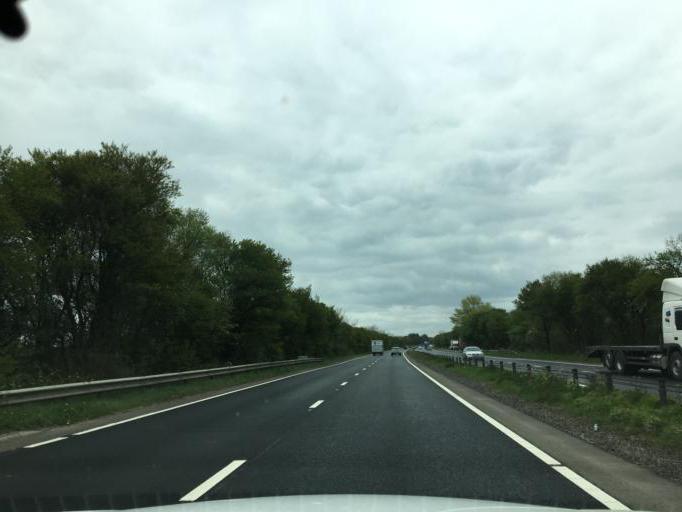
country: GB
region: Wales
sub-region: Carmarthenshire
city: Llangynog
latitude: 51.8380
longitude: -4.4228
